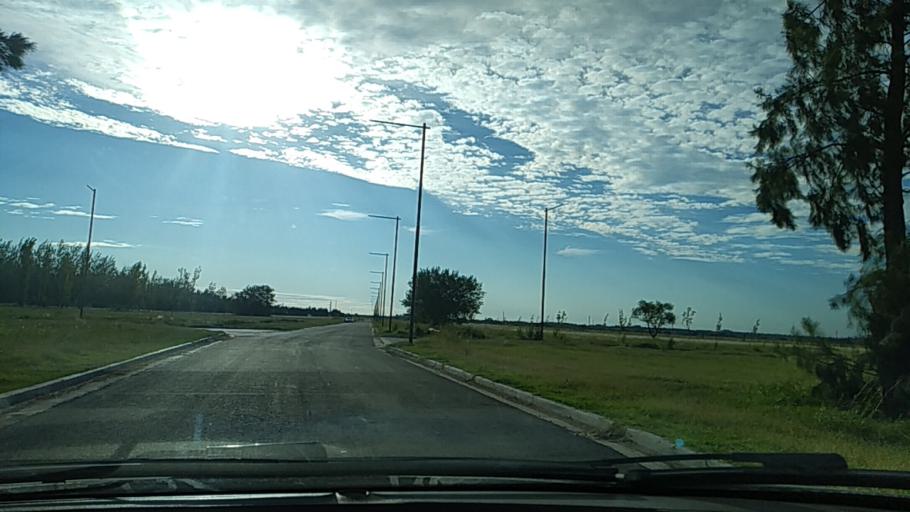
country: AR
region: Santa Fe
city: Perez
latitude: -32.9469
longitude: -60.7679
